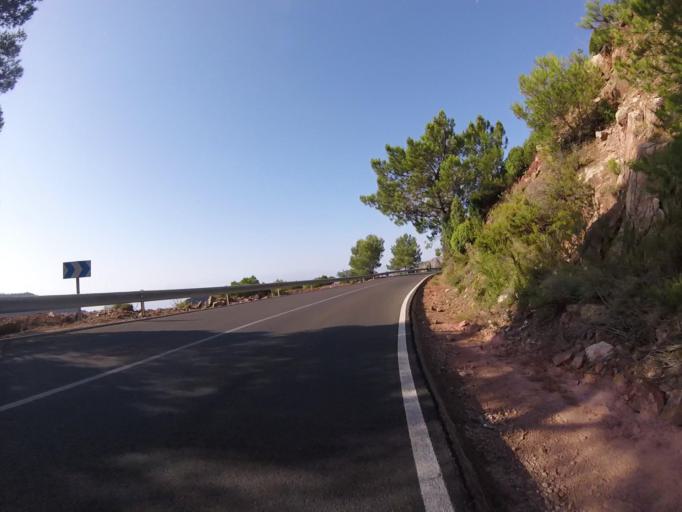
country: ES
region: Valencia
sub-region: Provincia de Castello
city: Benicassim
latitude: 40.0790
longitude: 0.0393
